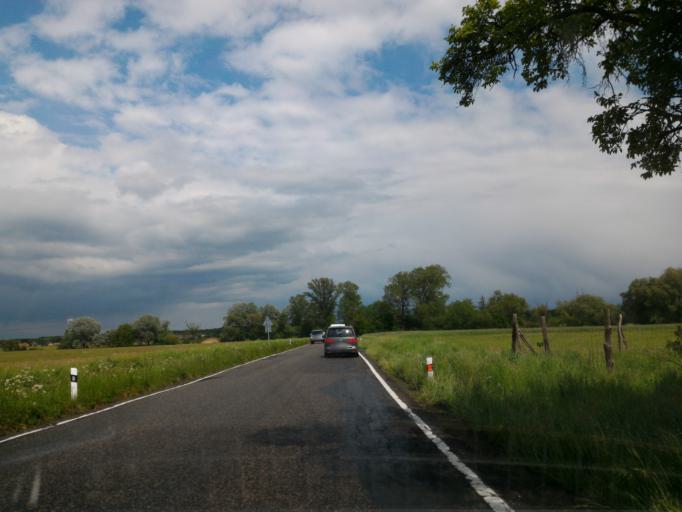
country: CZ
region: Central Bohemia
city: Velim
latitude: 50.0754
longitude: 15.1391
